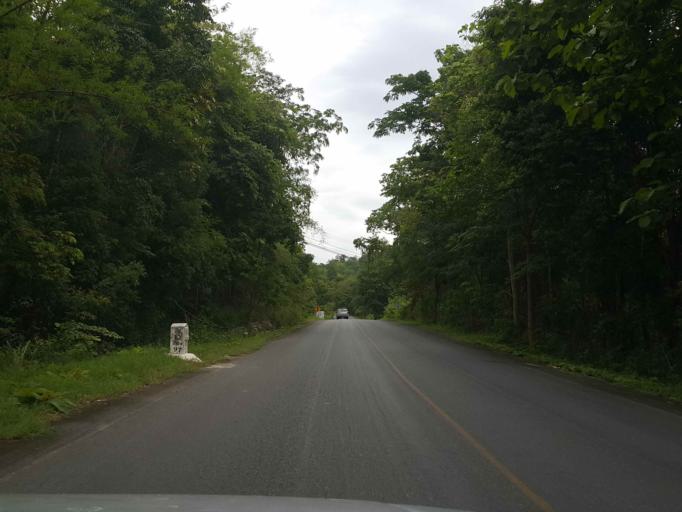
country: TH
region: Lampang
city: Thoen
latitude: 17.6088
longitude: 99.3255
